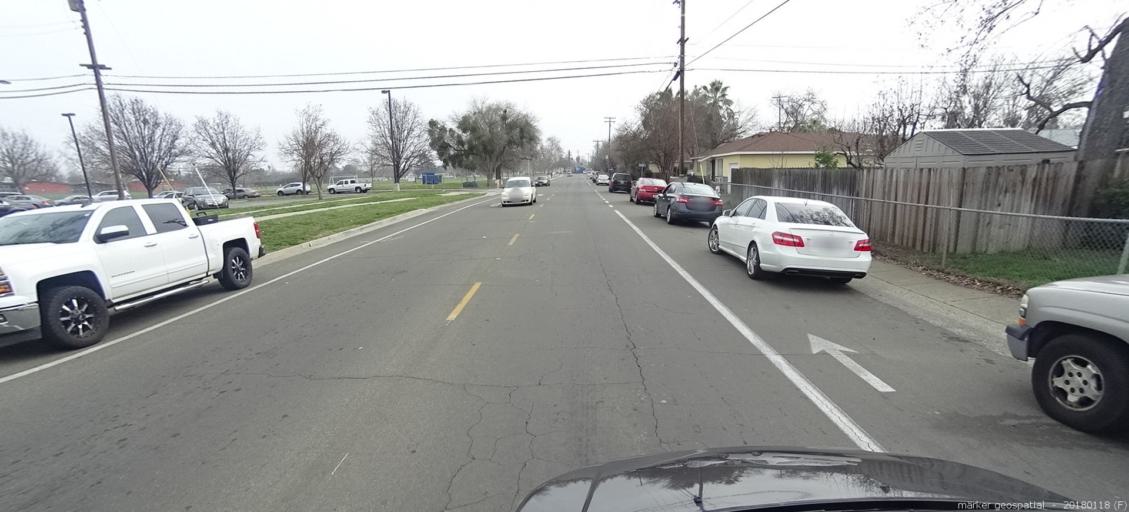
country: US
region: California
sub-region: Sacramento County
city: Rancho Cordova
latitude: 38.5983
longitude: -121.3077
